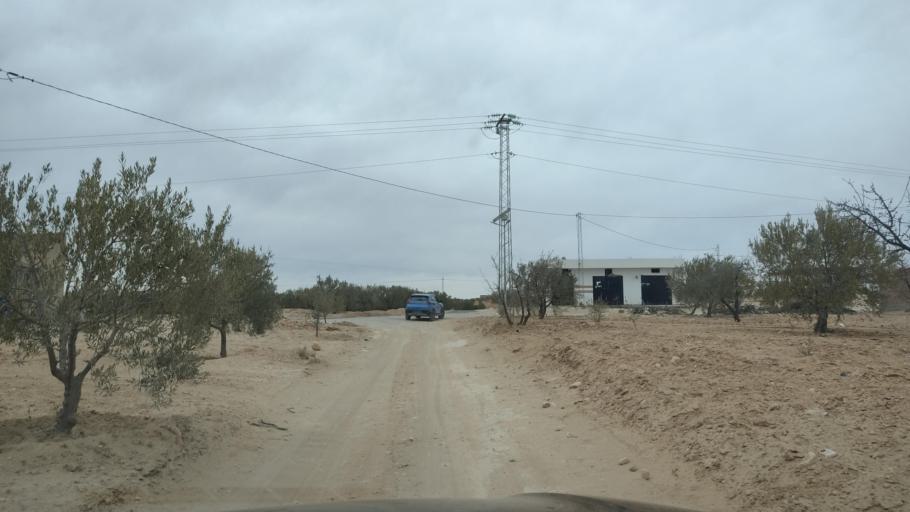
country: TN
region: Al Qasrayn
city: Kasserine
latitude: 35.2303
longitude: 8.9101
